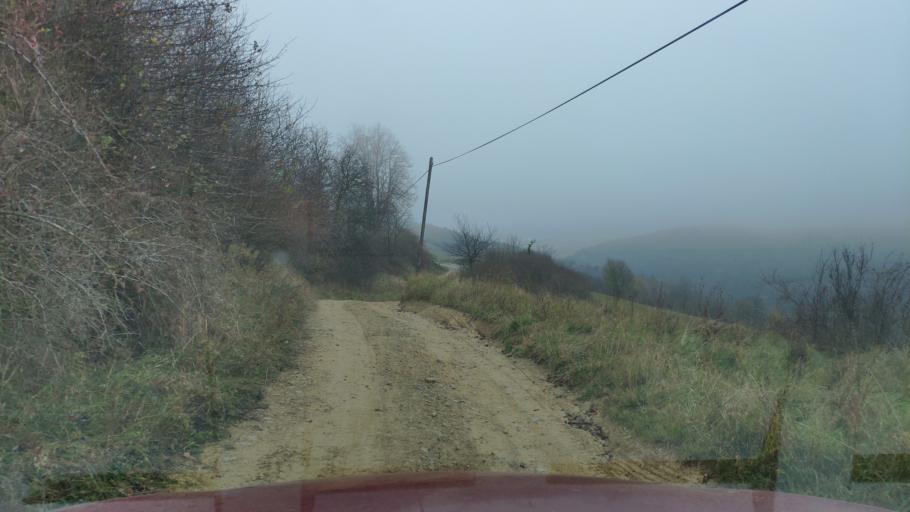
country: SK
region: Presovsky
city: Sabinov
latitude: 49.1361
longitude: 21.2276
